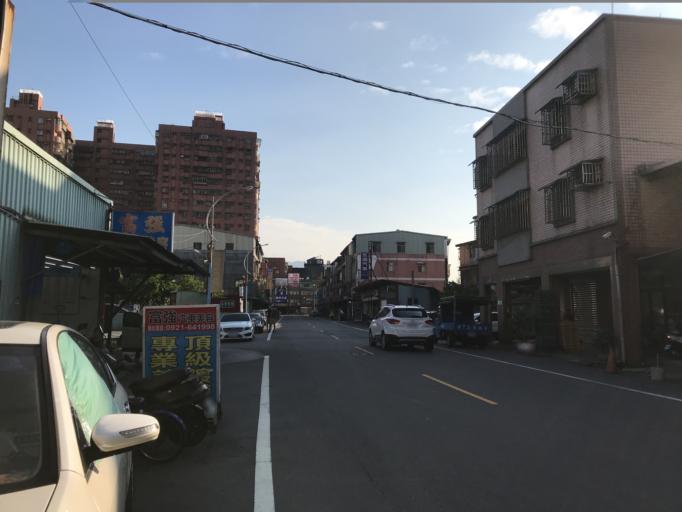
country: TW
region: Taiwan
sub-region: Taoyuan
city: Taoyuan
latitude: 24.9288
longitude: 121.3713
